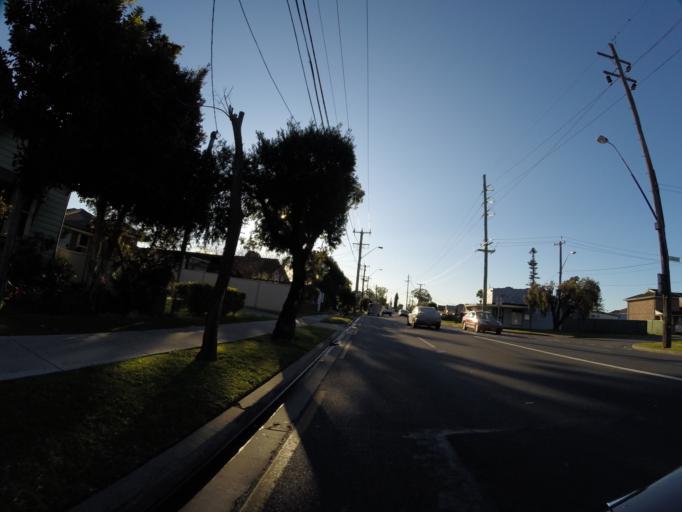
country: AU
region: New South Wales
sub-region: Fairfield
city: Fairfield Heights
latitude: -33.8628
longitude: 150.9534
